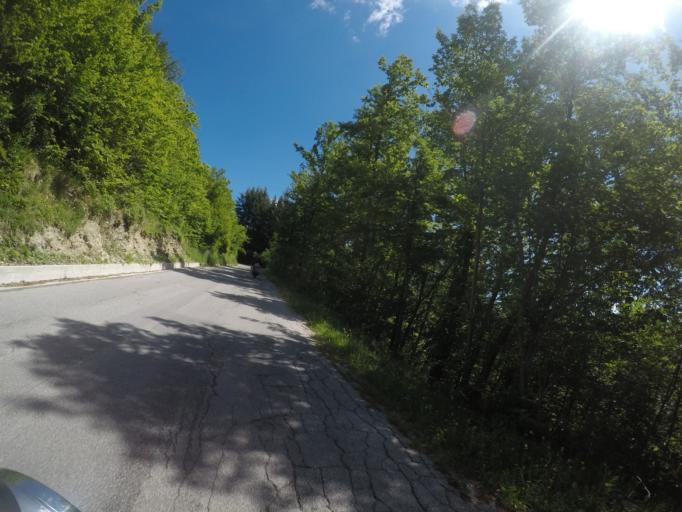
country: IT
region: Tuscany
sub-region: Provincia di Lucca
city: Careggine
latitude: 44.0964
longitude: 10.3266
